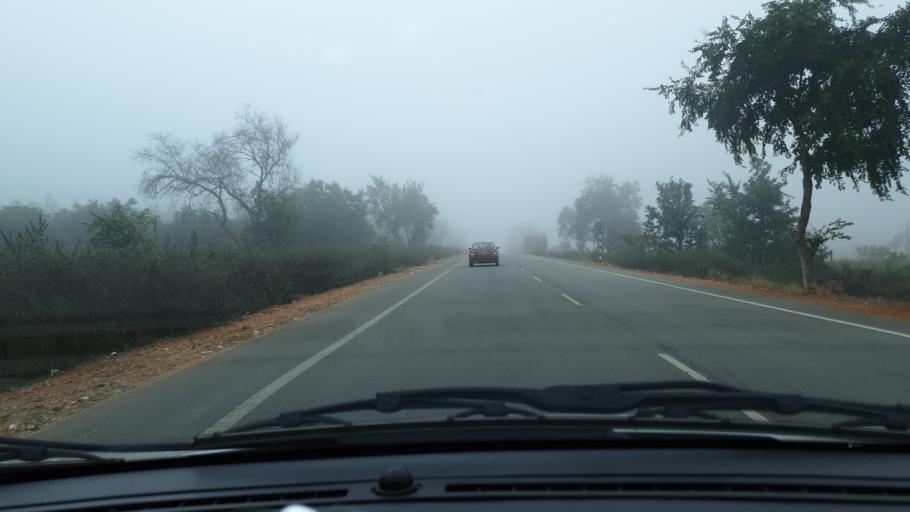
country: IN
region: Telangana
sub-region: Mahbubnagar
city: Nagar Karnul
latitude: 16.6584
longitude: 78.5765
